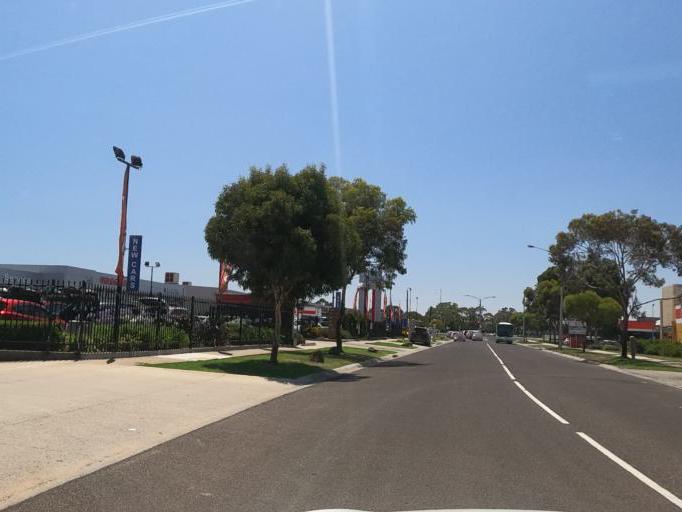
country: AU
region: Victoria
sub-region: Hume
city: Coolaroo
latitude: -37.6426
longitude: 144.9310
